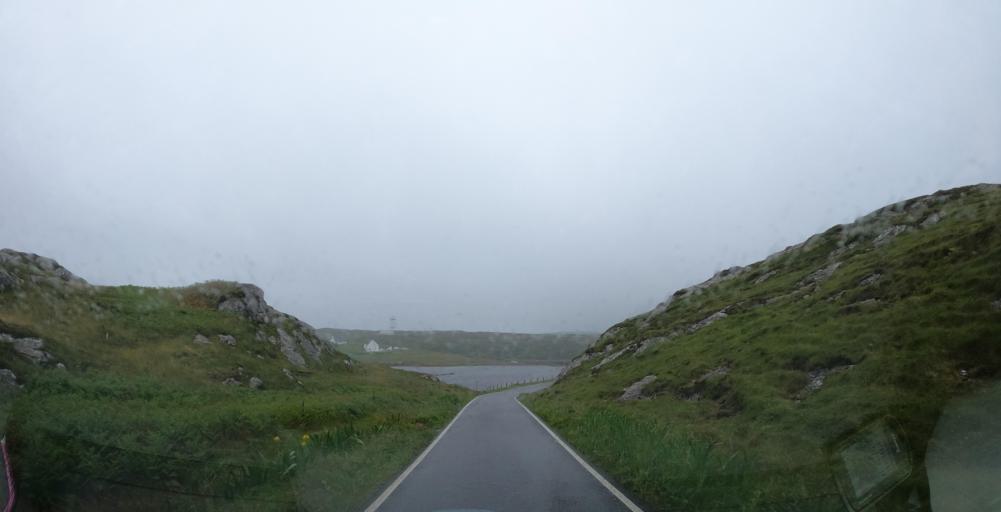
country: GB
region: Scotland
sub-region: Eilean Siar
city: Barra
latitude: 56.9928
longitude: -7.4190
